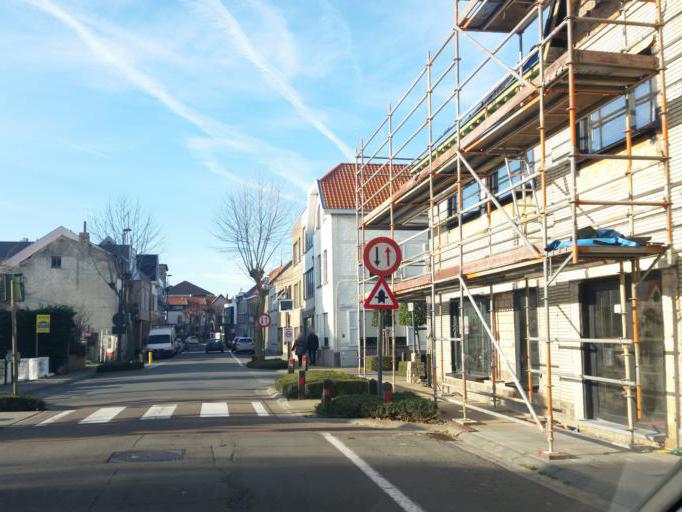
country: BE
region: Flanders
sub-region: Provincie West-Vlaanderen
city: De Haan
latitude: 51.2712
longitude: 3.0381
